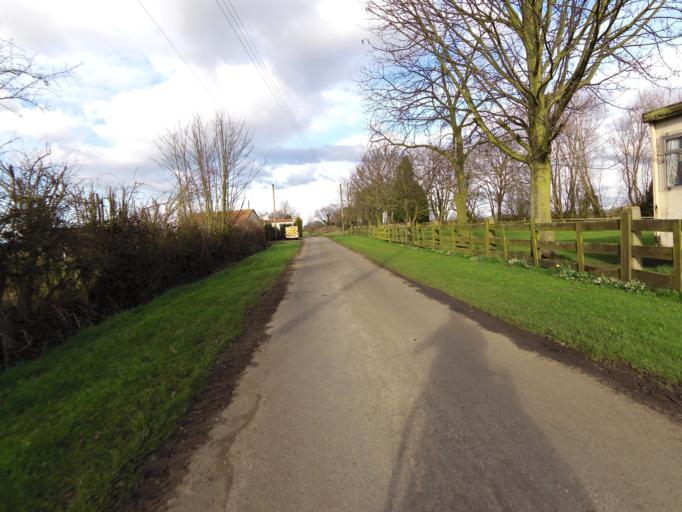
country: GB
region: England
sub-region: North Yorkshire
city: Brayton
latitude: 53.7191
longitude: -1.0823
